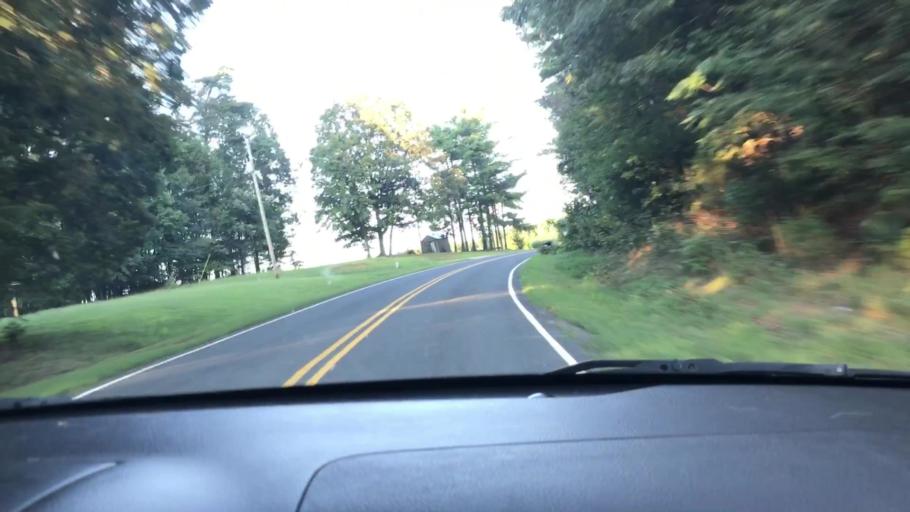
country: US
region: North Carolina
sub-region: Randolph County
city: Ramseur
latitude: 35.7775
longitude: -79.6243
